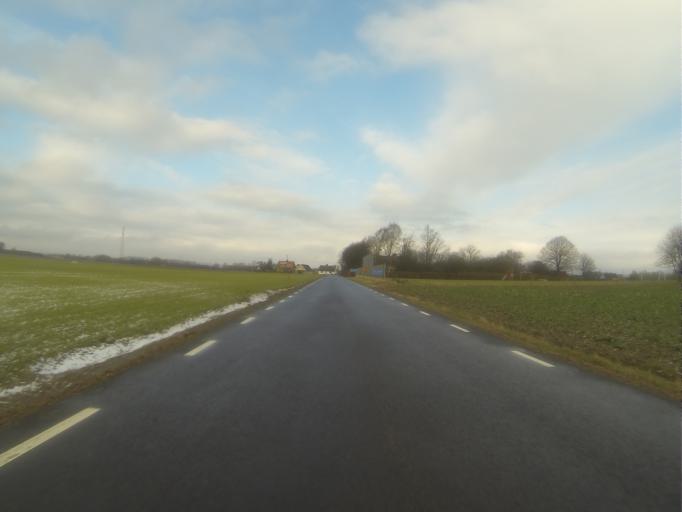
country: SE
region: Skane
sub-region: Svedala Kommun
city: Klagerup
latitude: 55.6221
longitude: 13.3100
